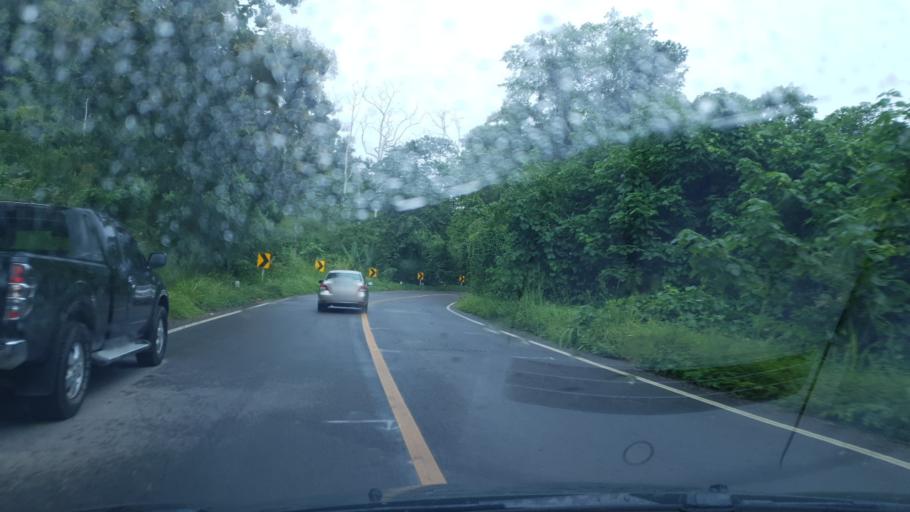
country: TH
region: Mae Hong Son
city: Khun Yuam
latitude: 18.6853
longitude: 97.9198
